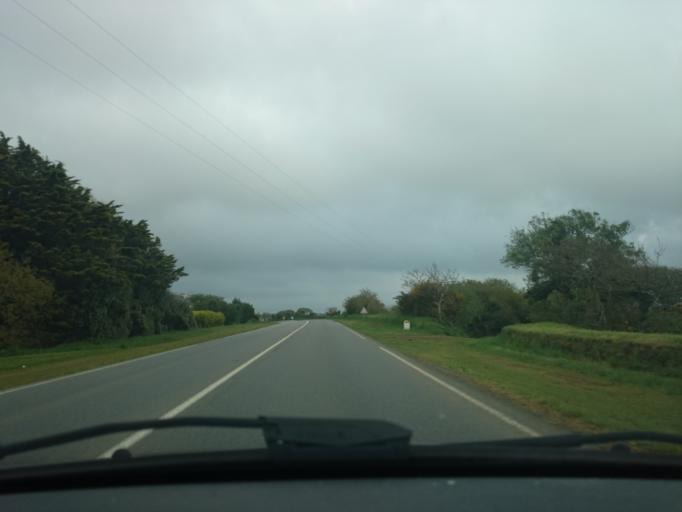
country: FR
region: Brittany
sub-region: Departement du Finistere
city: Lanrivoare
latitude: 48.4689
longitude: -4.6435
